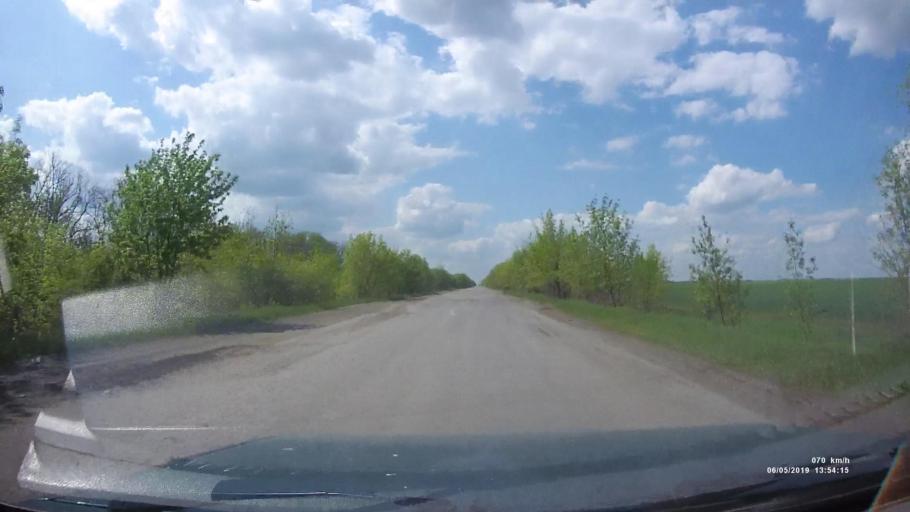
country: RU
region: Rostov
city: Melikhovskaya
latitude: 47.6734
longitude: 40.4498
